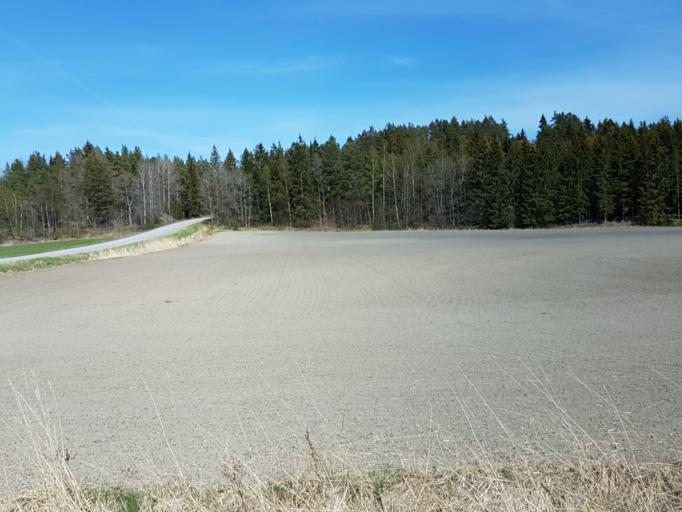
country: SE
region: Soedermanland
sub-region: Nykopings Kommun
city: Svalsta
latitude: 58.6411
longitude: 16.9222
